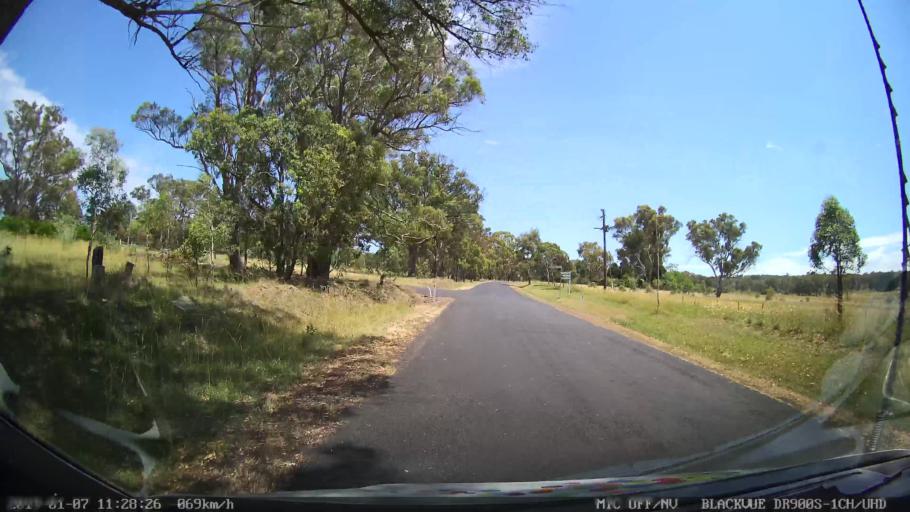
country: AU
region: New South Wales
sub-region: Armidale Dumaresq
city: Armidale
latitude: -30.4486
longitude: 151.5663
